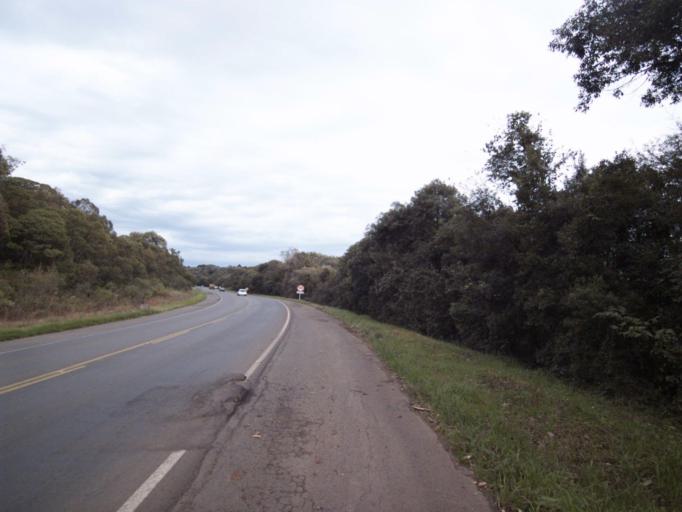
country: BR
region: Santa Catarina
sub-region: Concordia
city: Concordia
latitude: -26.9660
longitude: -51.8463
